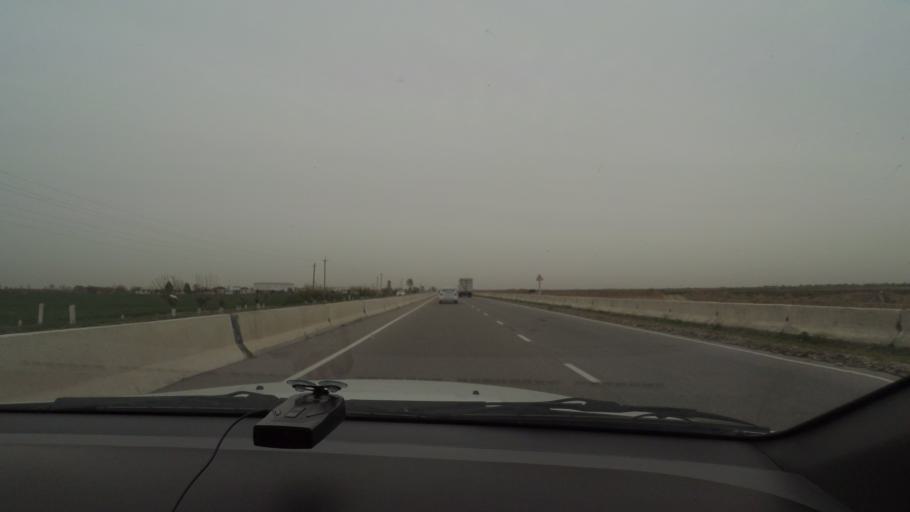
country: UZ
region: Jizzax
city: Gagarin
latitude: 40.4547
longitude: 68.2540
